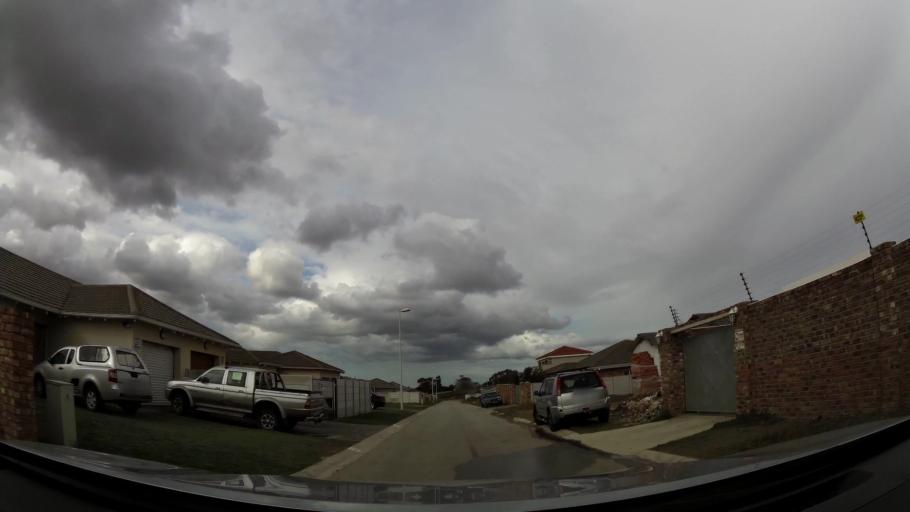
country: ZA
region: Eastern Cape
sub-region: Nelson Mandela Bay Metropolitan Municipality
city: Port Elizabeth
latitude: -33.9325
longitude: 25.5028
